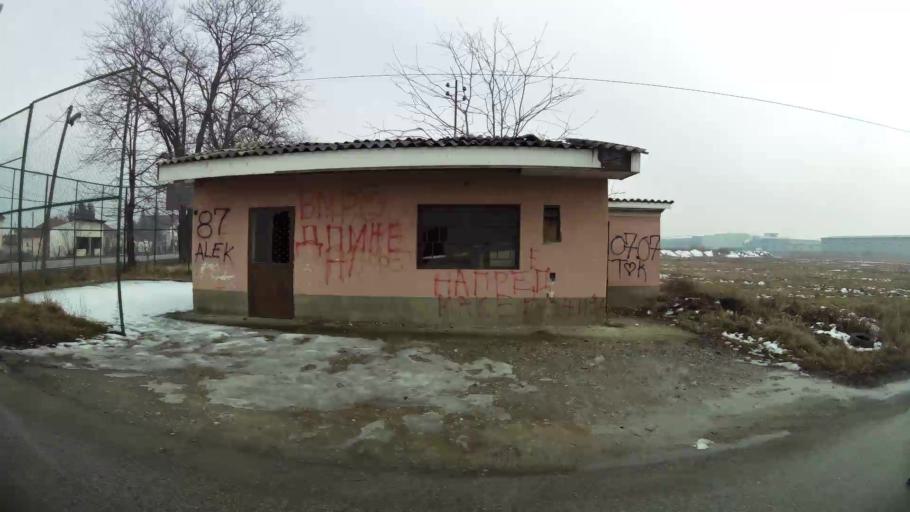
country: MK
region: Ilinden
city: Ilinden
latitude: 41.9956
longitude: 21.5649
